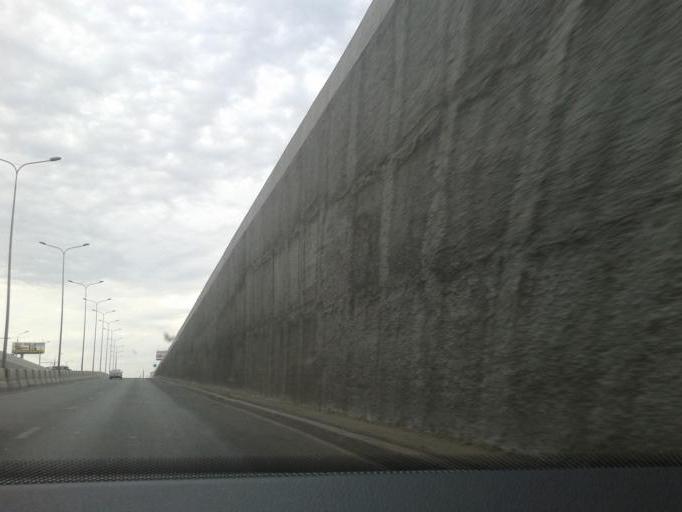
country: RU
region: Volgograd
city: Volgograd
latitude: 48.6366
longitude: 44.4304
